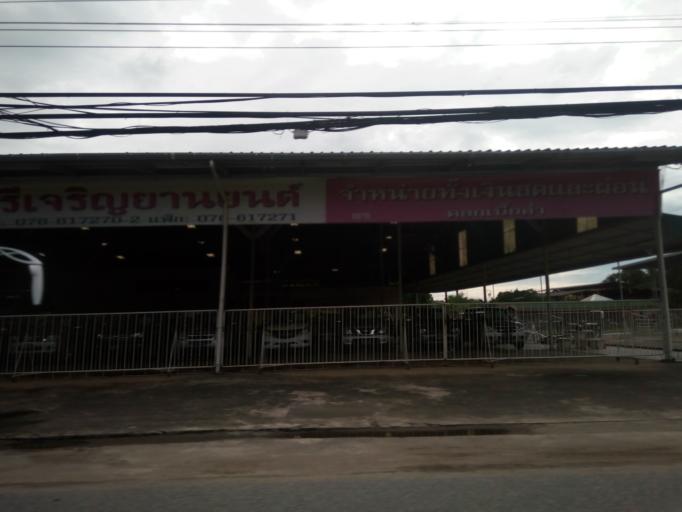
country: TH
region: Phuket
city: Thalang
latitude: 8.0009
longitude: 98.3474
